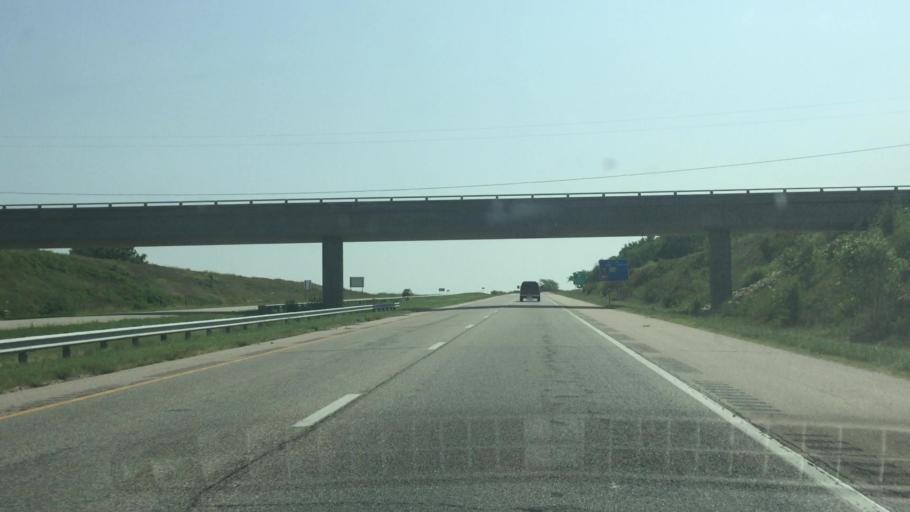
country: US
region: Kansas
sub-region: Osage County
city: Lyndon
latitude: 38.4260
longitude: -95.7481
